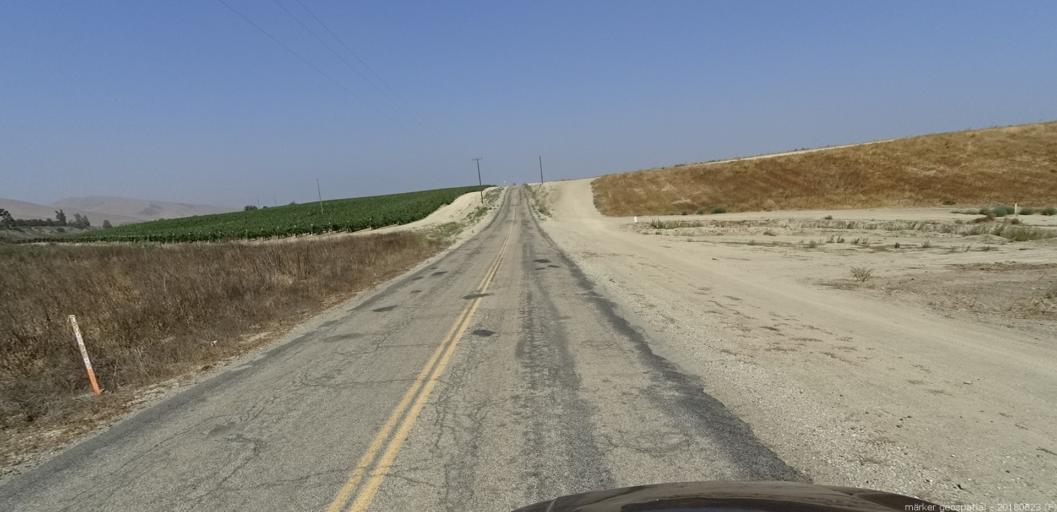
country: US
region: California
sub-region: Monterey County
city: Greenfield
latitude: 36.2585
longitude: -121.2055
